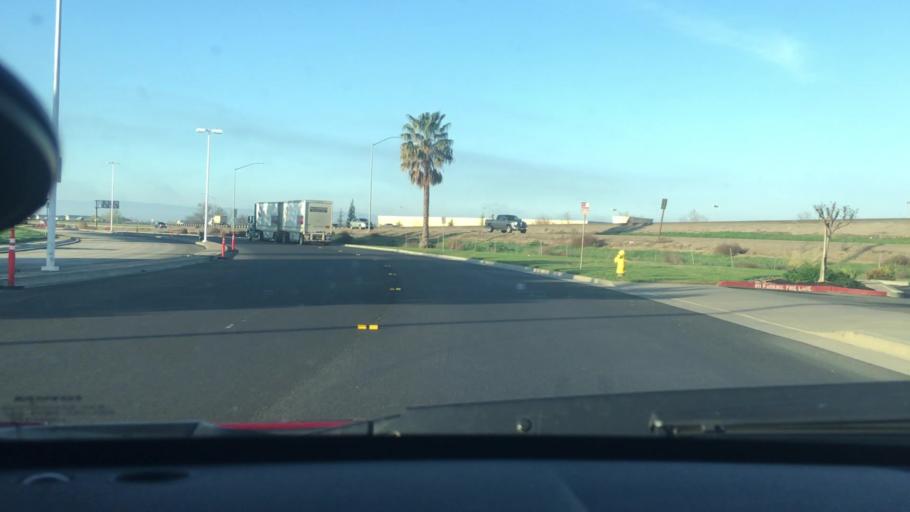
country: US
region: California
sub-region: San Joaquin County
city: Lathrop
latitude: 37.8098
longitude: -121.2953
